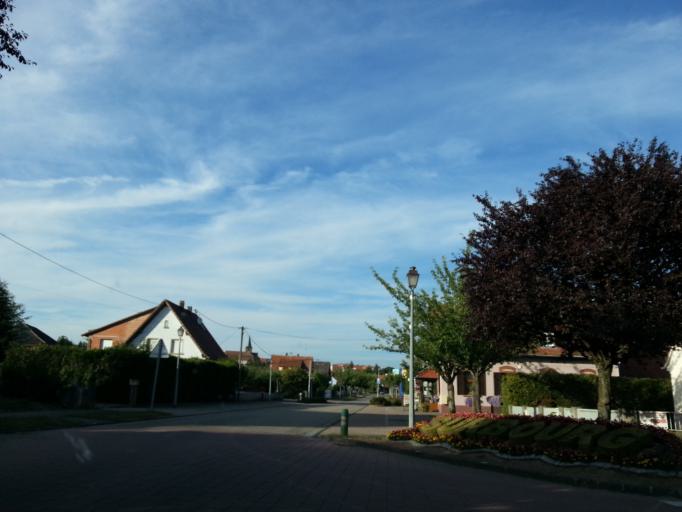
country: FR
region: Alsace
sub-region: Departement du Bas-Rhin
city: Surbourg
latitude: 48.9042
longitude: 7.8432
